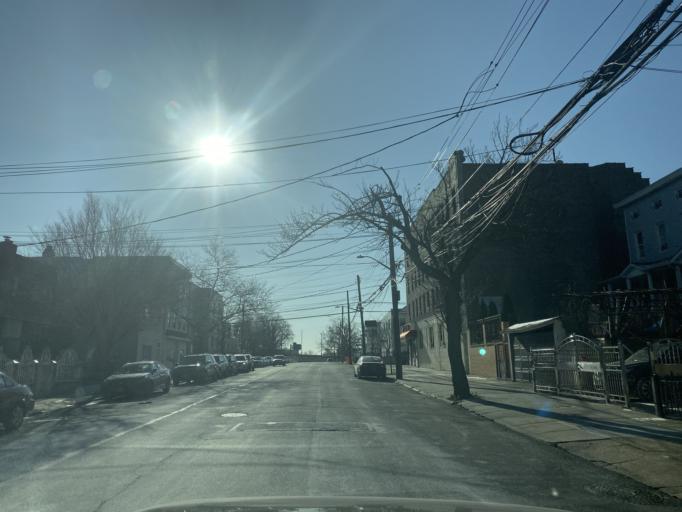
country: US
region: New York
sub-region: Bronx
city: The Bronx
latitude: 40.8315
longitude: -73.8479
